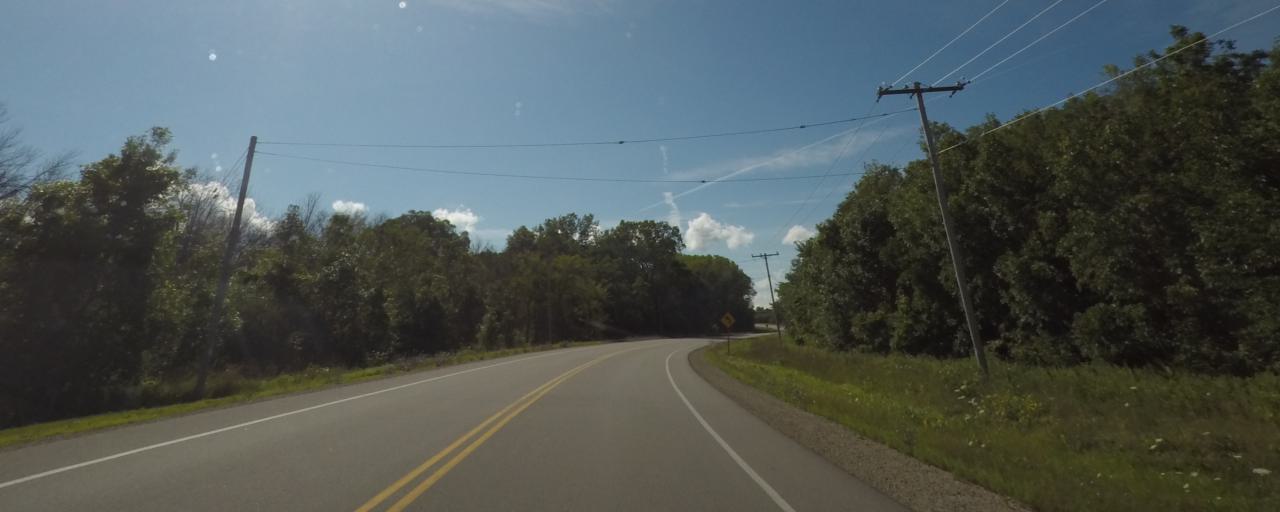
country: US
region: Wisconsin
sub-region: Jefferson County
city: Ixonia
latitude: 43.0727
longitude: -88.6372
